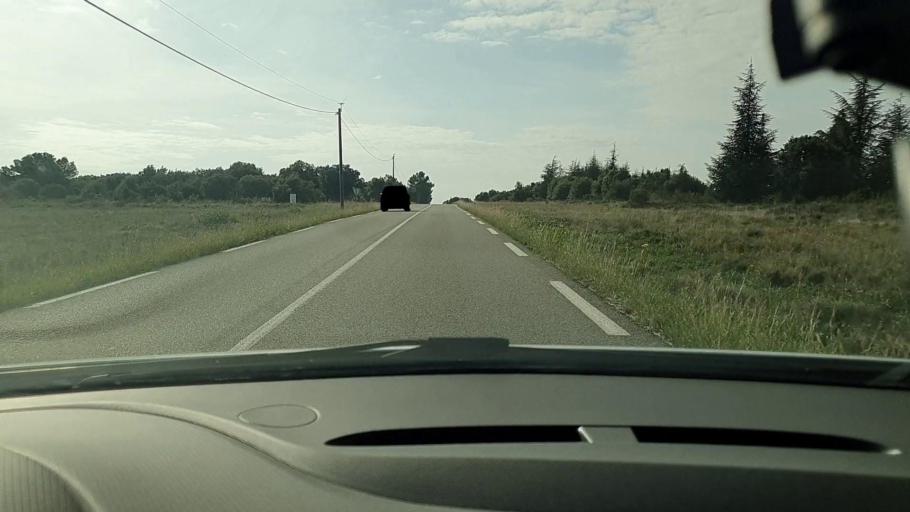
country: FR
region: Languedoc-Roussillon
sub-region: Departement du Gard
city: Montaren-et-Saint-Mediers
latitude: 44.0829
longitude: 4.3914
